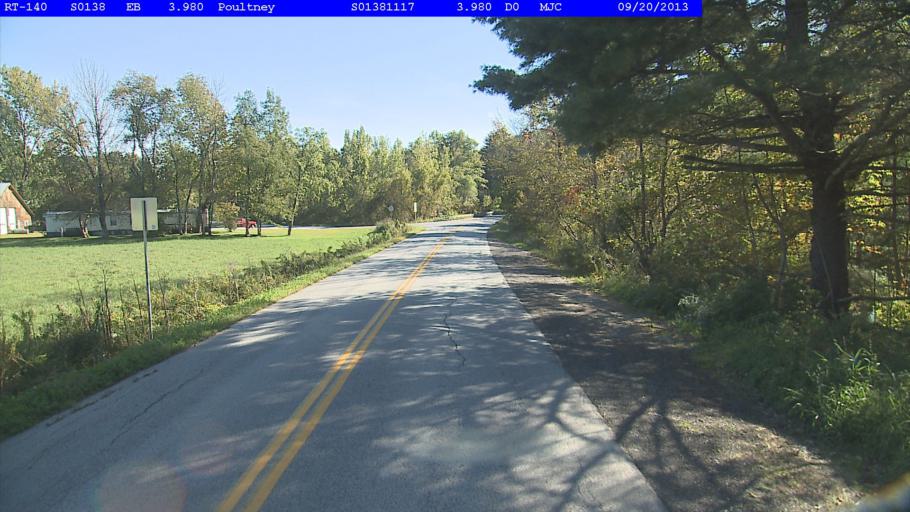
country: US
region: Vermont
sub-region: Rutland County
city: Poultney
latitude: 43.5084
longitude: -73.1778
